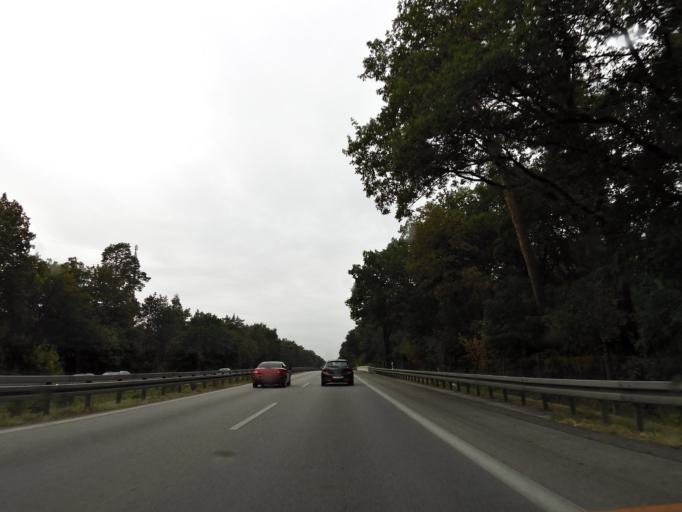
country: DE
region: Berlin
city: Zehlendorf Bezirk
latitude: 52.4626
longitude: 13.2280
